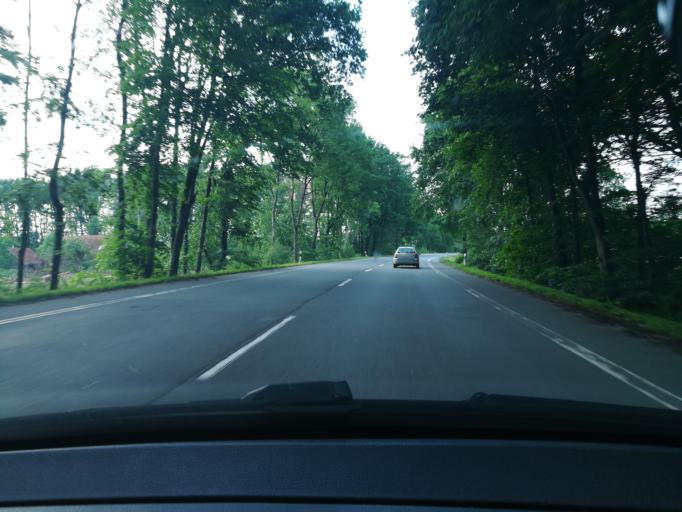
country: DE
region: North Rhine-Westphalia
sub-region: Regierungsbezirk Detmold
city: Oerlinghausen
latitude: 51.8953
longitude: 8.6708
